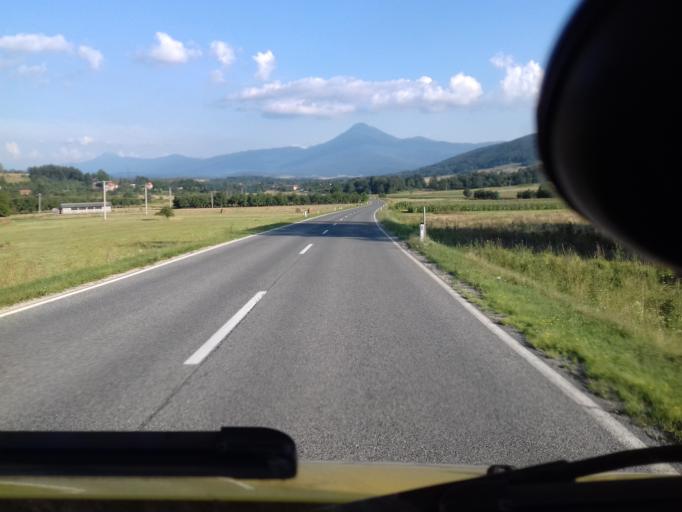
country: BA
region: Federation of Bosnia and Herzegovina
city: Orasac
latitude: 44.6466
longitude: 16.1655
